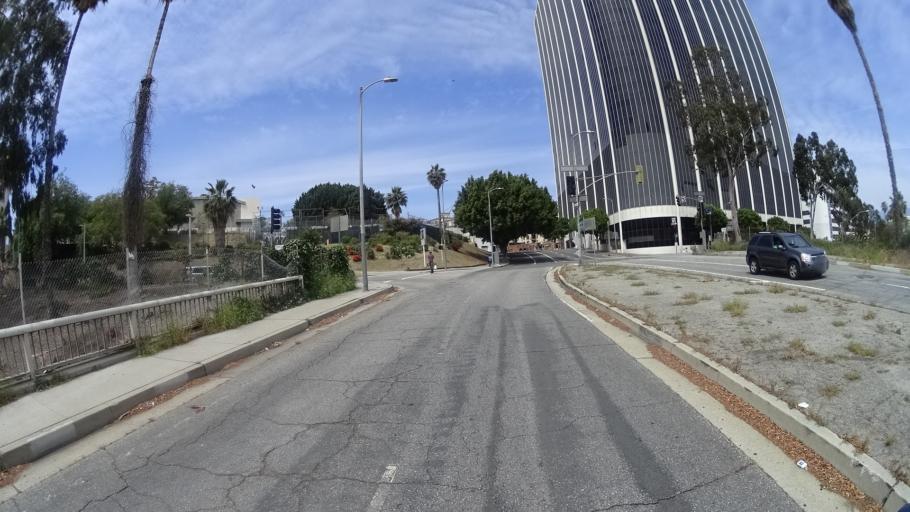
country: US
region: California
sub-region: Los Angeles County
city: Los Angeles
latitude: 34.0553
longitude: -118.2574
